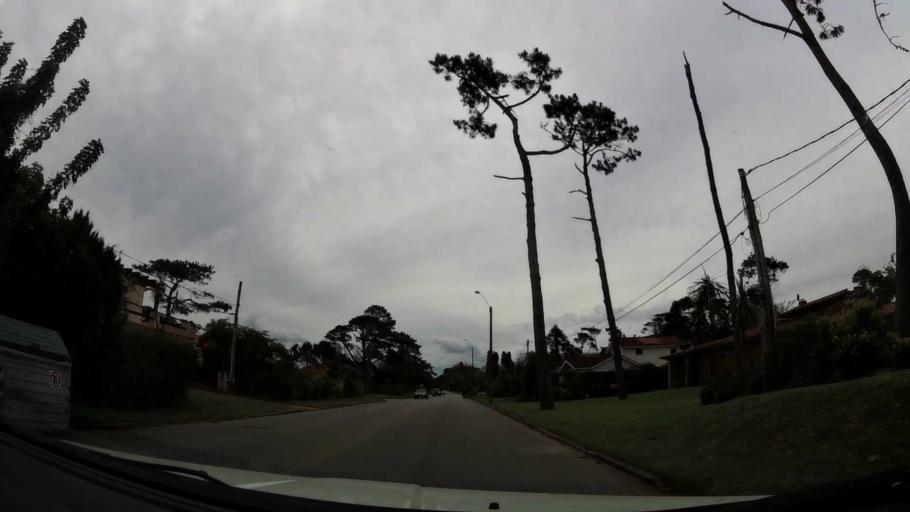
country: UY
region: Maldonado
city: Punta del Este
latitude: -34.9357
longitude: -54.9478
